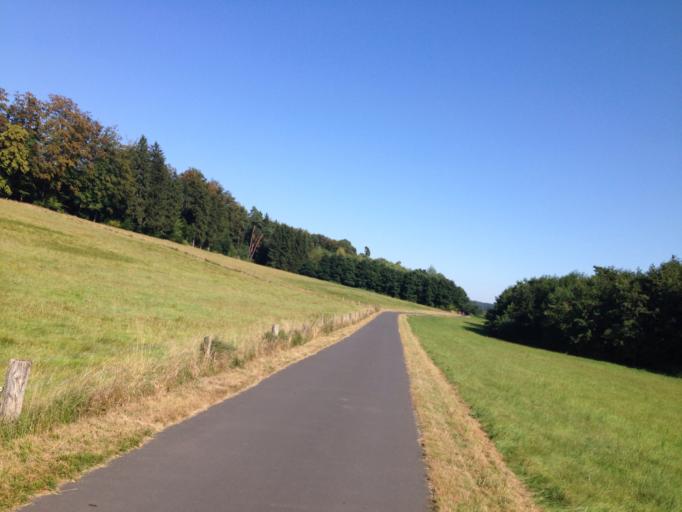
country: DE
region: Hesse
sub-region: Regierungsbezirk Giessen
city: Rabenau
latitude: 50.6424
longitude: 8.9066
